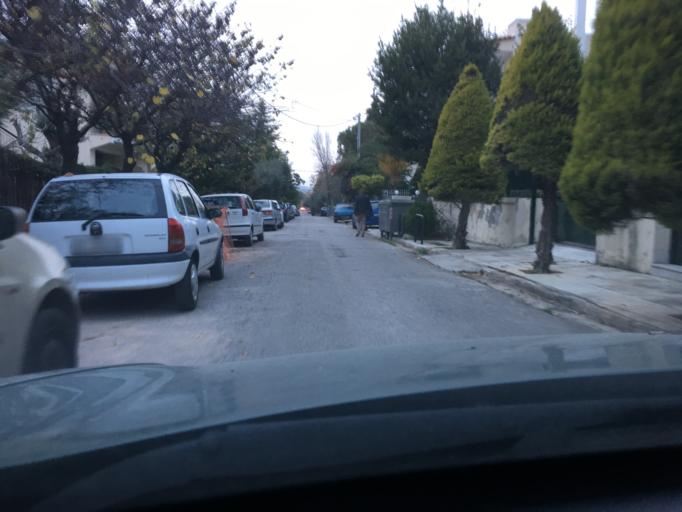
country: GR
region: Attica
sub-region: Nomarchia Athinas
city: Khalandrion
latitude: 38.0262
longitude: 23.8029
